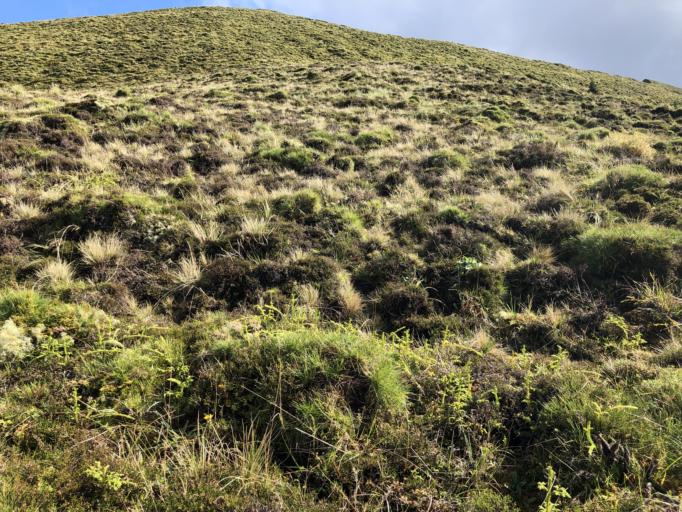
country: PT
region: Azores
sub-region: Ponta Delgada
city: Arrifes
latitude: 37.8296
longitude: -25.7576
